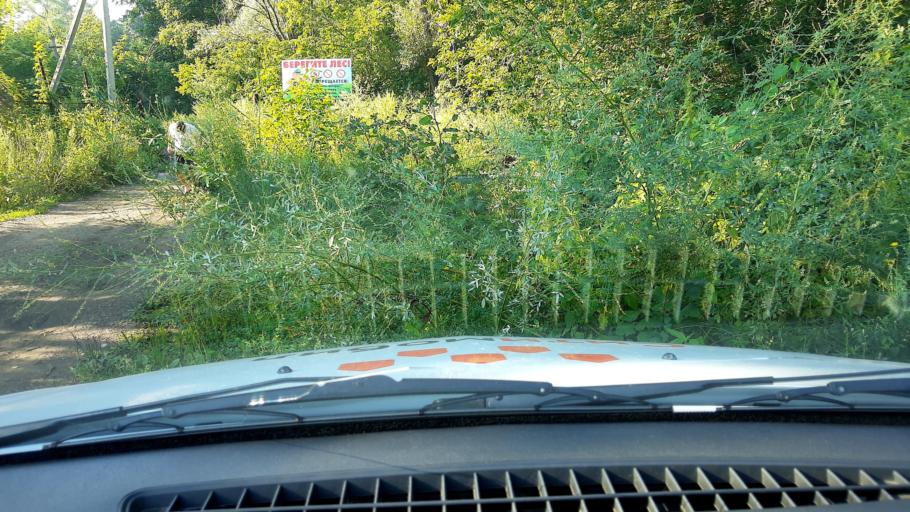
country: RU
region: Bashkortostan
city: Mikhaylovka
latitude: 54.6901
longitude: 55.8494
